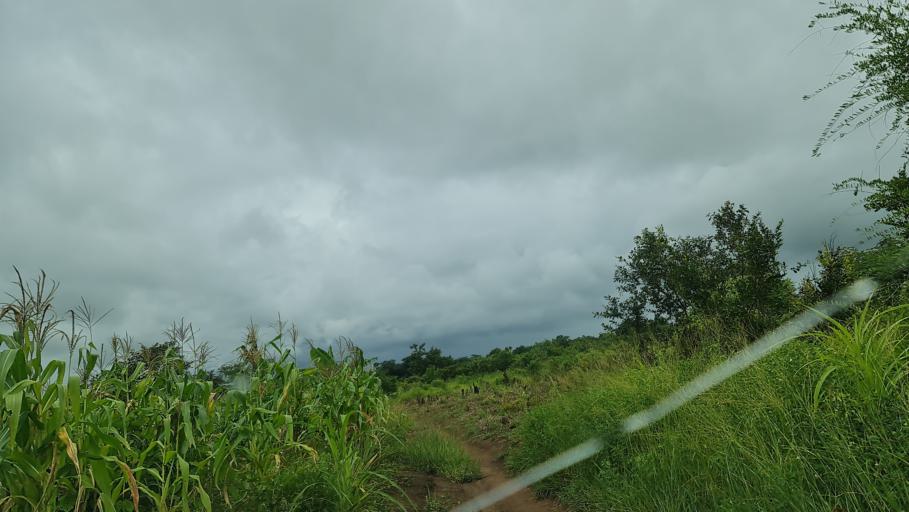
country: MW
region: Southern Region
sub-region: Nsanje District
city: Nsanje
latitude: -17.3937
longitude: 35.7848
